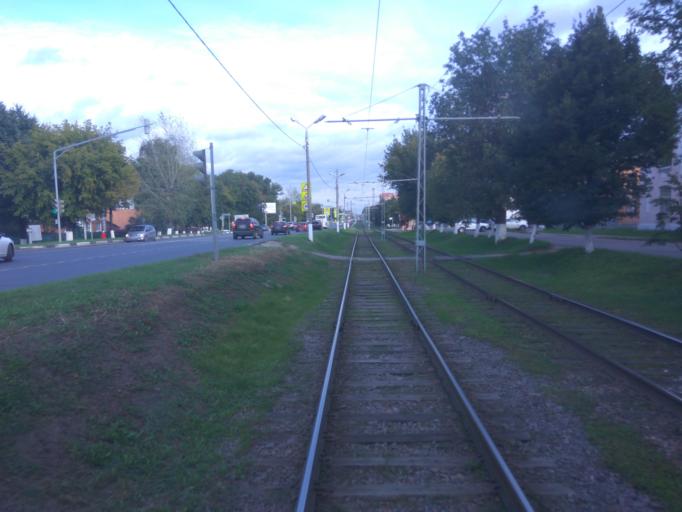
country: RU
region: Moskovskaya
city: Kolomna
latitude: 55.0880
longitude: 38.7890
